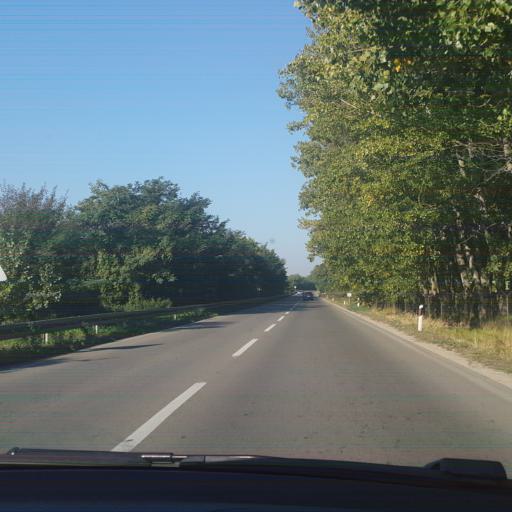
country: RS
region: Central Serbia
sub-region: Toplicki Okrug
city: Prokuplje
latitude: 43.2332
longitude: 21.5362
